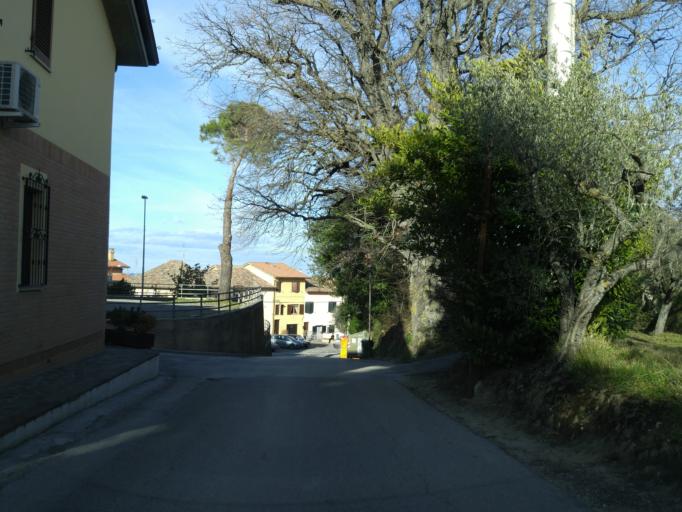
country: IT
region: The Marches
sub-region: Provincia di Pesaro e Urbino
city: Cartoceto
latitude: 43.7640
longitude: 12.8833
